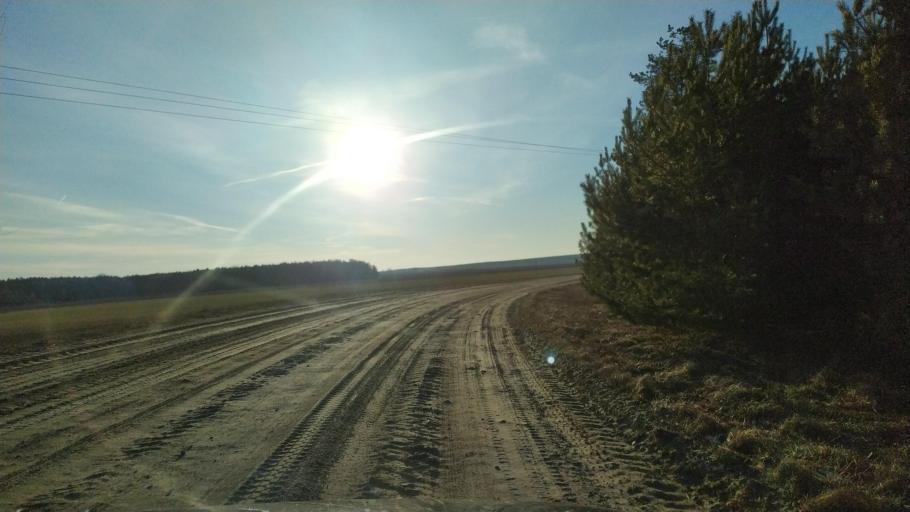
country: BY
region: Brest
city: Pruzhany
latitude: 52.5457
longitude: 24.2841
